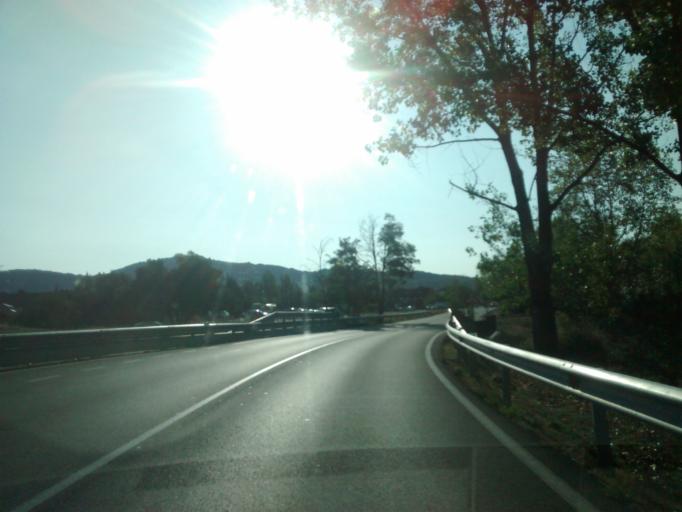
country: ES
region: Madrid
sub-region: Provincia de Madrid
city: Collado-Villalba
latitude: 40.6523
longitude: -4.0030
